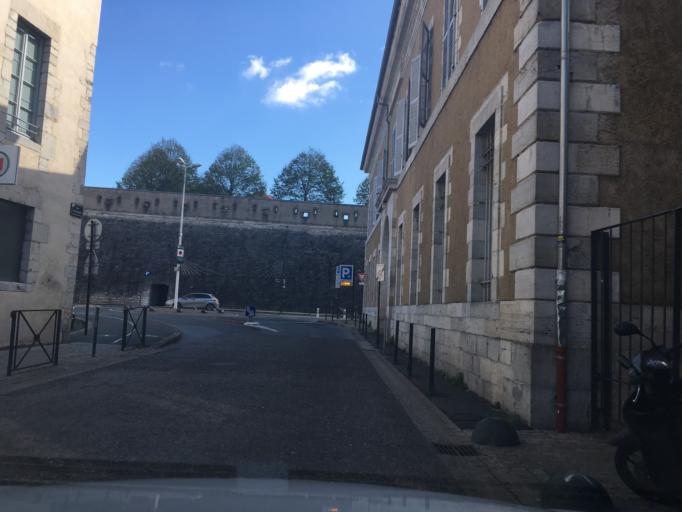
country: FR
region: Aquitaine
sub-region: Departement des Pyrenees-Atlantiques
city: Bayonne
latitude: 43.4890
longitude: -1.4721
